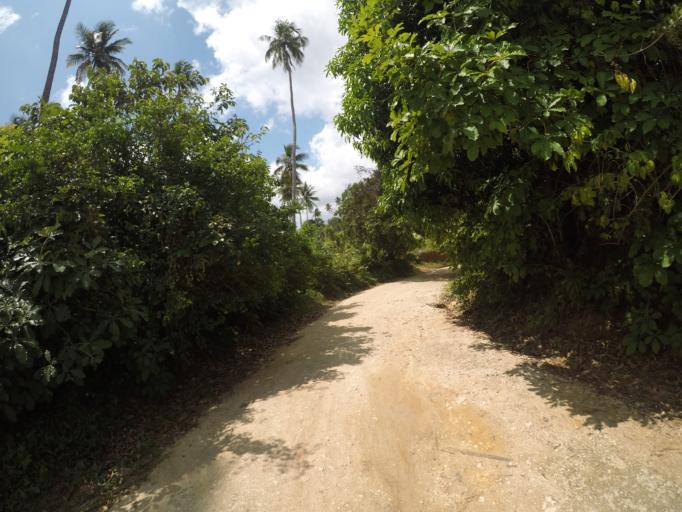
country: TZ
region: Pemba South
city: Mtambile
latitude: -5.3865
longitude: 39.7430
